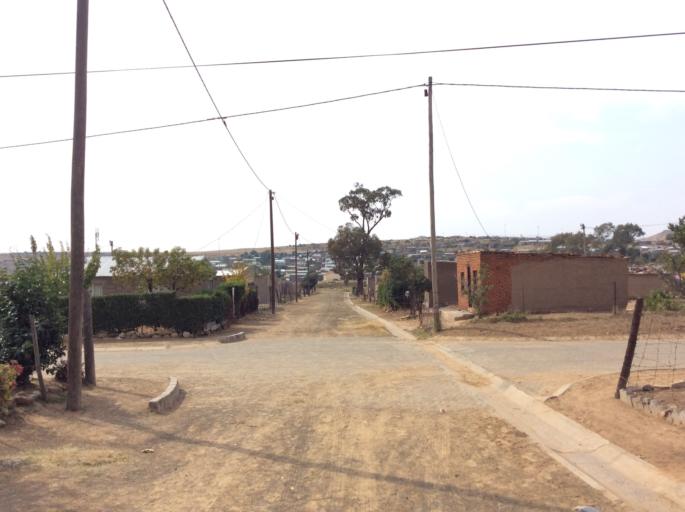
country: ZA
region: Orange Free State
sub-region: Xhariep District Municipality
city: Dewetsdorp
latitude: -29.5886
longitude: 26.6753
